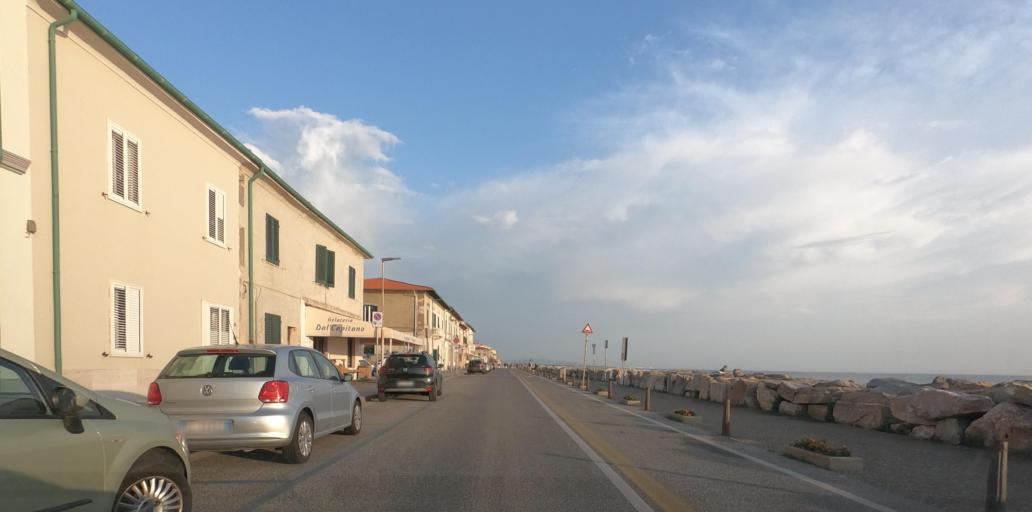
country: IT
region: Tuscany
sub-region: Province of Pisa
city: Marina di Pisa
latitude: 43.6696
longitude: 10.2739
